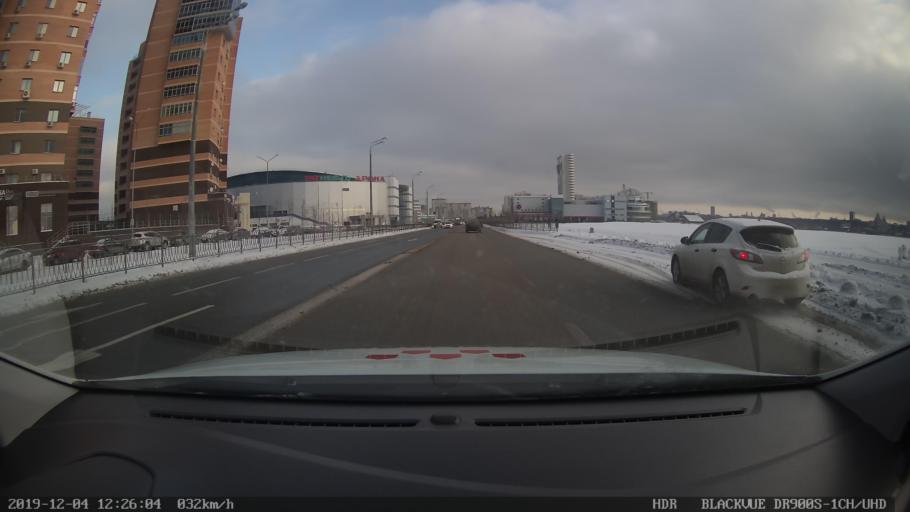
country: RU
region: Tatarstan
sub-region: Gorod Kazan'
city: Kazan
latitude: 55.8158
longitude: 49.1221
